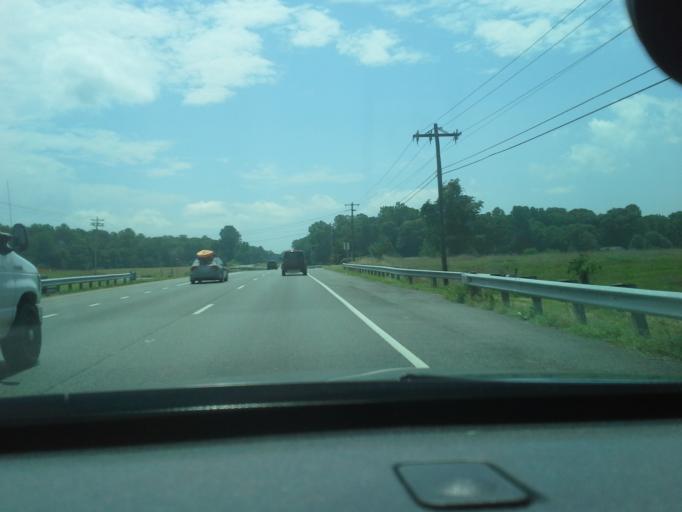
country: US
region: Maryland
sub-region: Calvert County
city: Huntingtown Town Center
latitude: 38.6452
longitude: -76.6061
